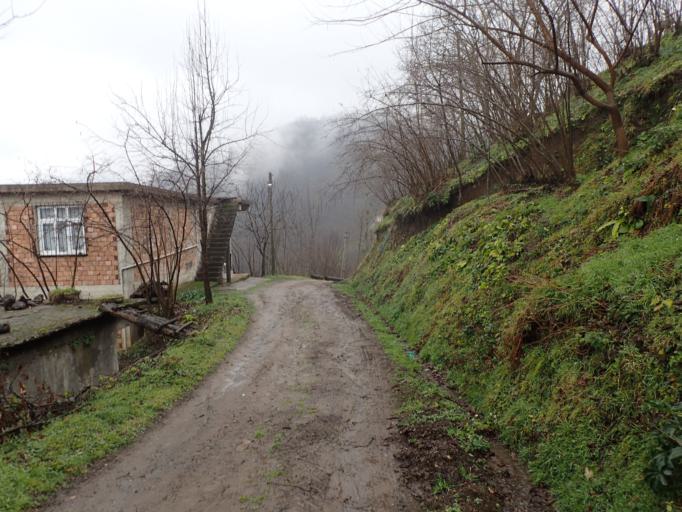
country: TR
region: Ordu
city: Camas
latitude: 40.9131
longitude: 37.5716
